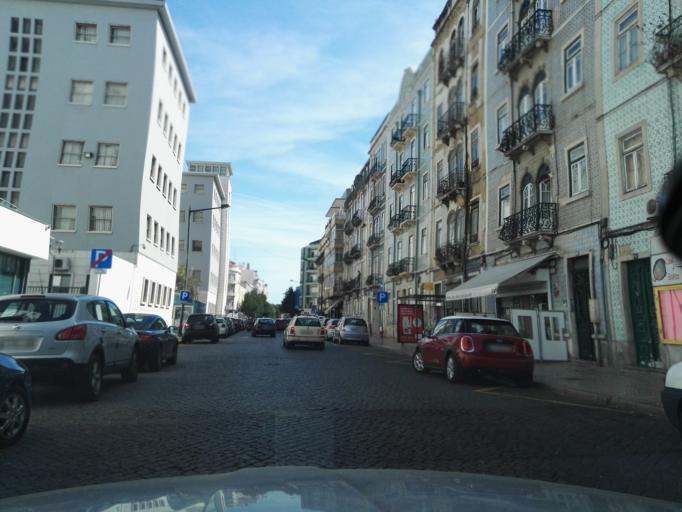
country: PT
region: Lisbon
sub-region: Lisbon
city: Lisbon
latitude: 38.7286
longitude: -9.1431
